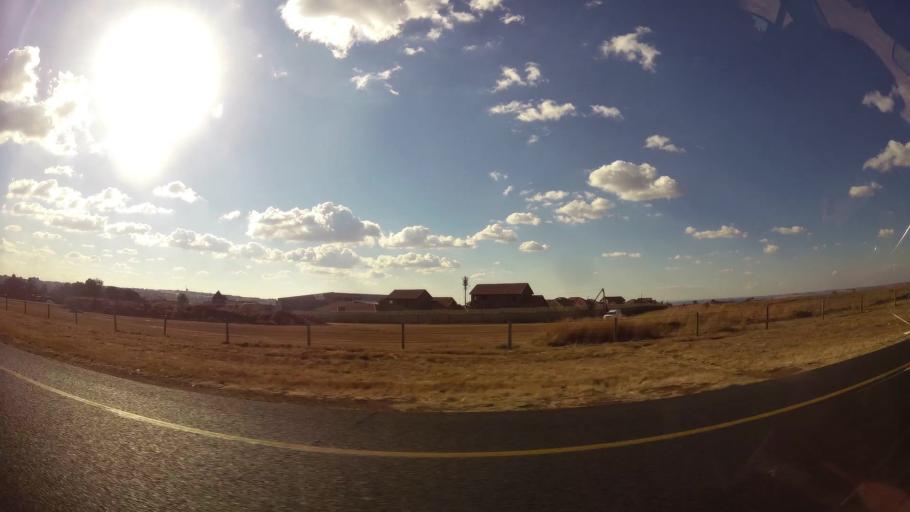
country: ZA
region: Mpumalanga
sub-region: Nkangala District Municipality
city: Witbank
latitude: -25.8956
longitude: 29.2540
